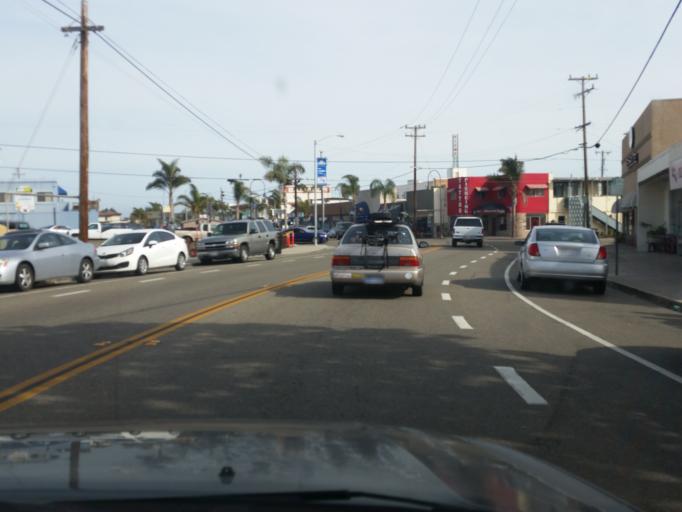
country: US
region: California
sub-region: San Luis Obispo County
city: Pismo Beach
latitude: 35.1419
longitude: -120.6423
